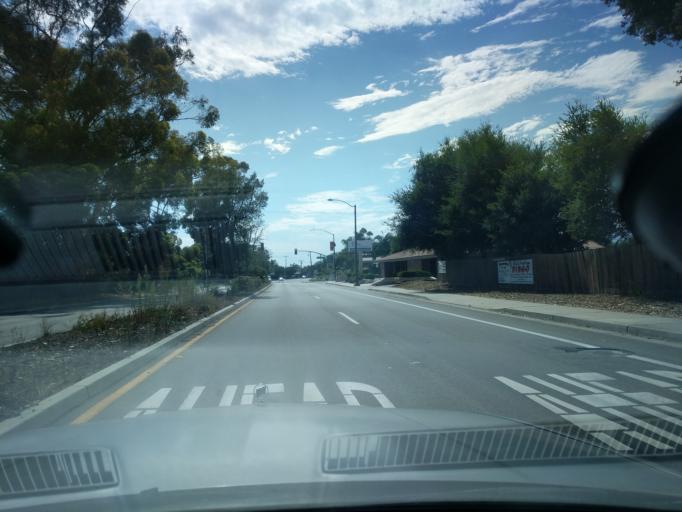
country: US
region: California
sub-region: Santa Barbara County
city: Goleta
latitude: 34.4413
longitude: -119.8185
